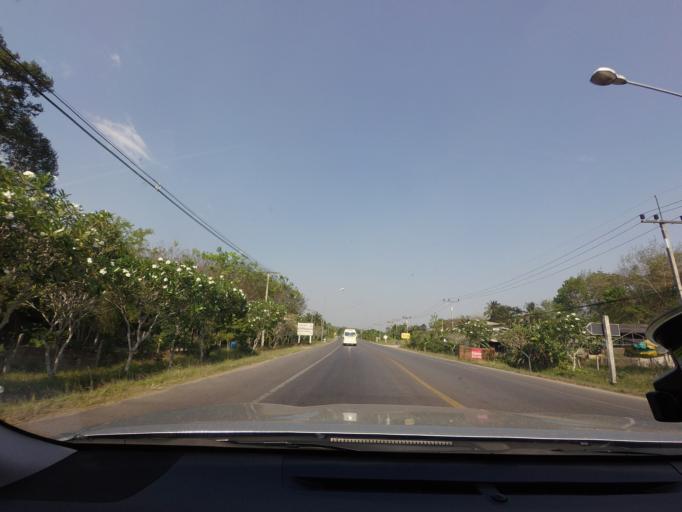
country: TH
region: Surat Thani
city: Phrasaeng
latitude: 8.5725
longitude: 99.2067
